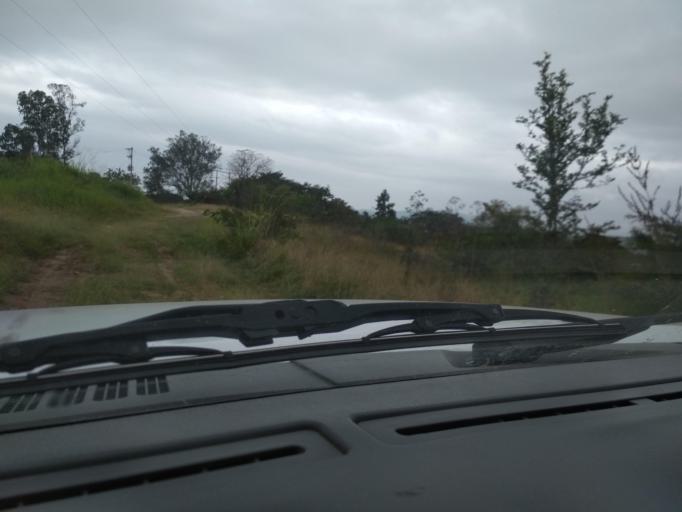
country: MX
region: Veracruz
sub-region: Emiliano Zapata
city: Dos Rios
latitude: 19.5203
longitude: -96.7938
